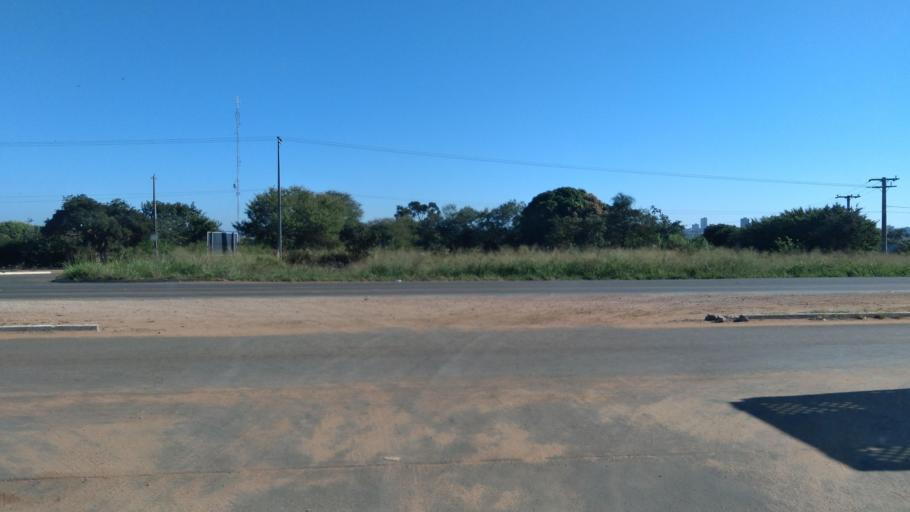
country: BR
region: Goias
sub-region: Mineiros
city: Mineiros
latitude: -17.5883
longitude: -52.5570
